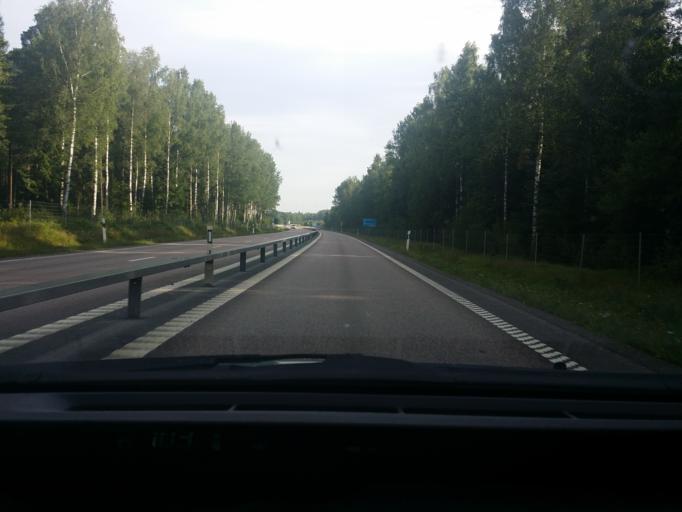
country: SE
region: Vaestmanland
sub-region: Vasteras
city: Hokasen
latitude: 59.6710
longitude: 16.5822
